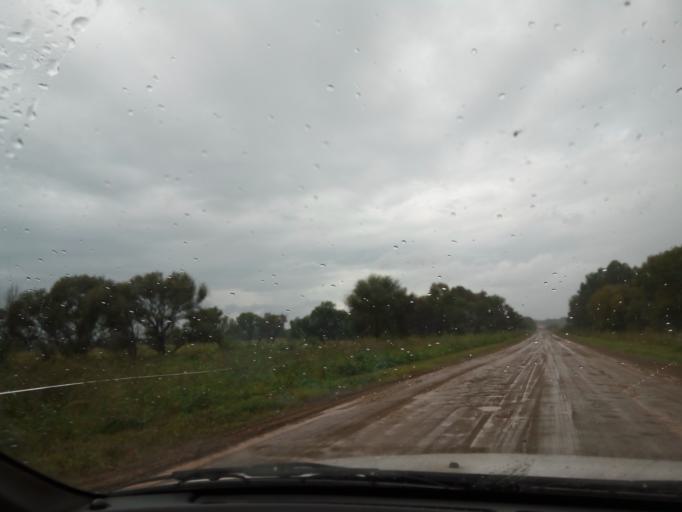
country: RU
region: Primorskiy
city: Lazo
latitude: 45.8472
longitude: 133.6451
